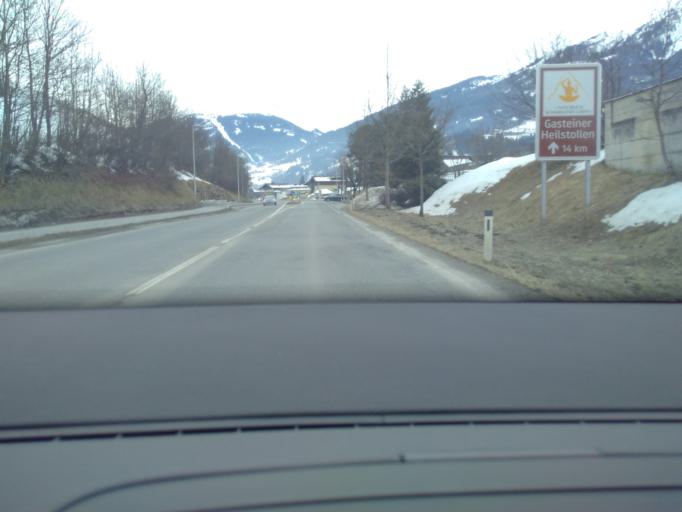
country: AT
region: Salzburg
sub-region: Politischer Bezirk Sankt Johann im Pongau
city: Bad Hofgastein
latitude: 47.1873
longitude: 13.1012
